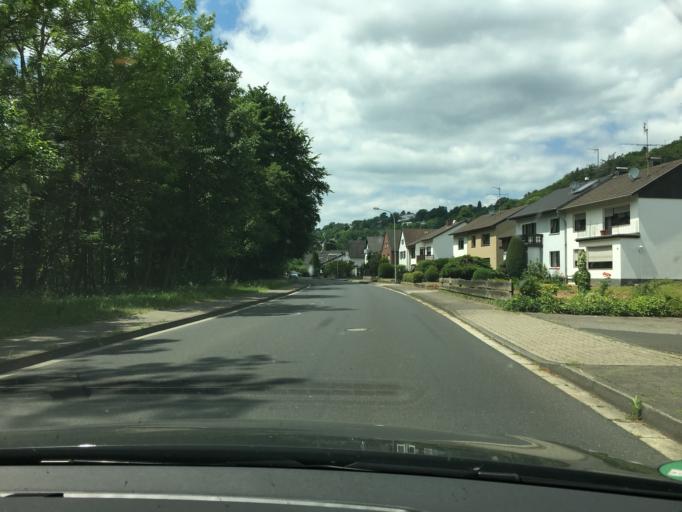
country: DE
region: North Rhine-Westphalia
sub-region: Regierungsbezirk Koln
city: Kreuzau
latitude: 50.7284
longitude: 6.4650
